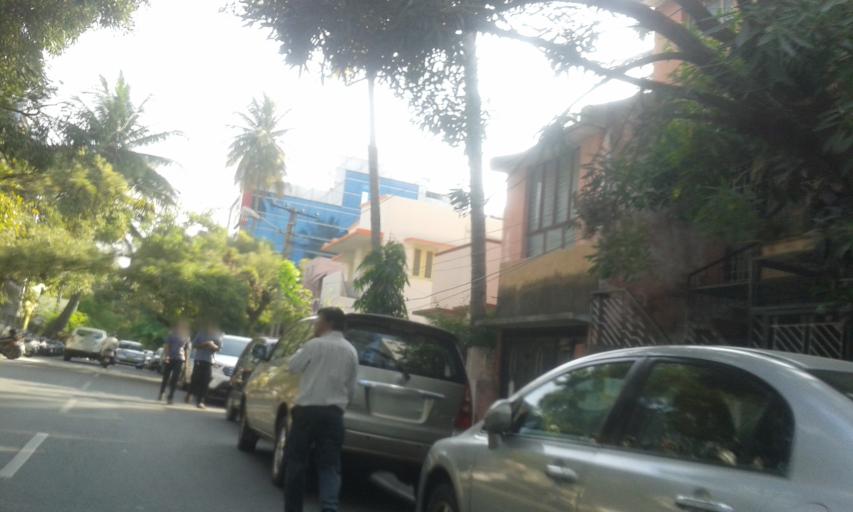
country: IN
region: Karnataka
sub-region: Bangalore Urban
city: Bangalore
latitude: 12.9315
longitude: 77.5866
